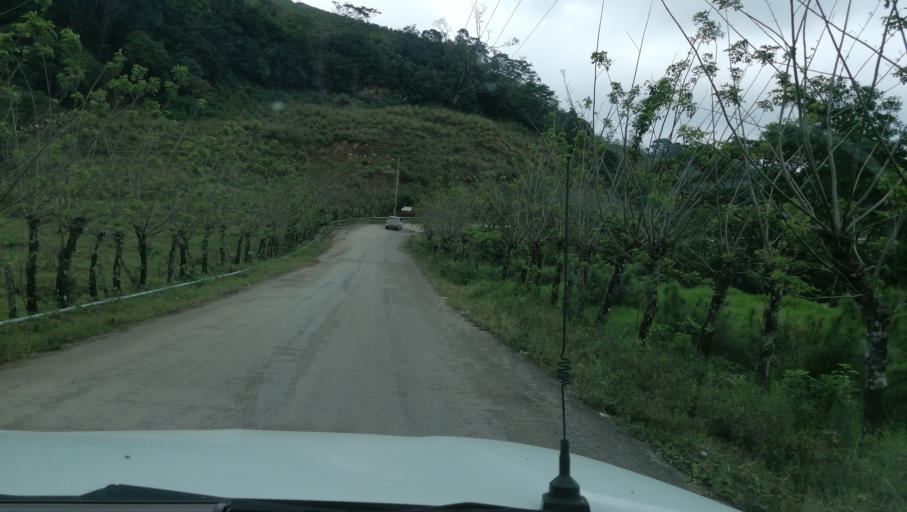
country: MX
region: Chiapas
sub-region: Francisco Leon
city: San Miguel la Sardina
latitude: 17.2790
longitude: -93.2741
